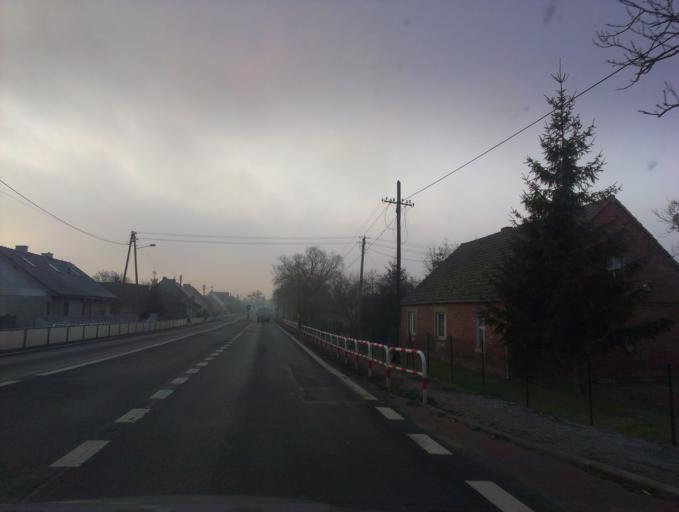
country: PL
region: Greater Poland Voivodeship
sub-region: Powiat obornicki
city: Rogozno
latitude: 52.8161
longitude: 16.9809
